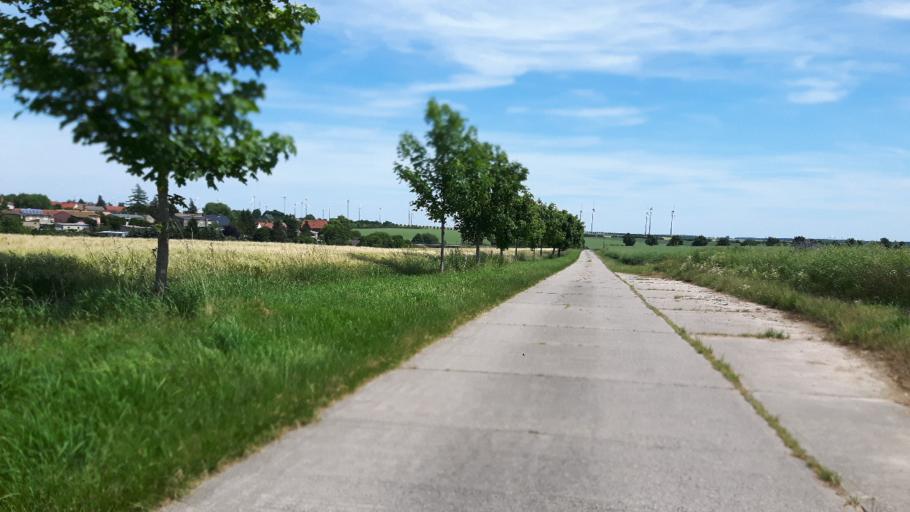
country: DE
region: Saxony-Anhalt
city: Kropstadt
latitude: 51.9983
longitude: 12.7664
